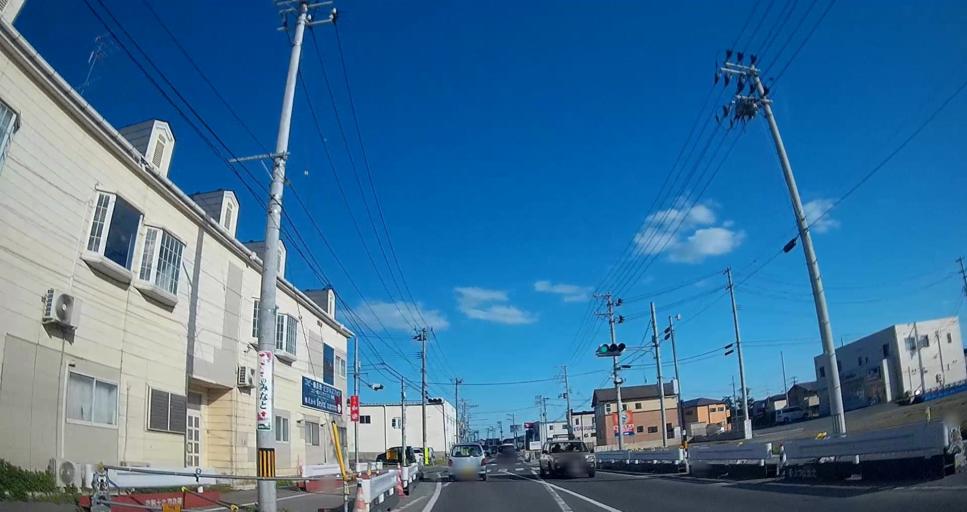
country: JP
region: Miyagi
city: Ishinomaki
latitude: 38.4251
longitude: 141.3174
